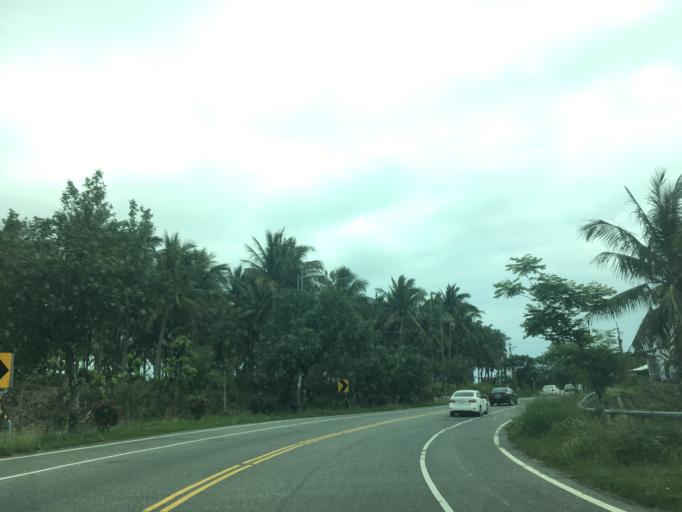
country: TW
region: Taiwan
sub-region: Taitung
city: Taitung
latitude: 22.9029
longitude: 121.2523
